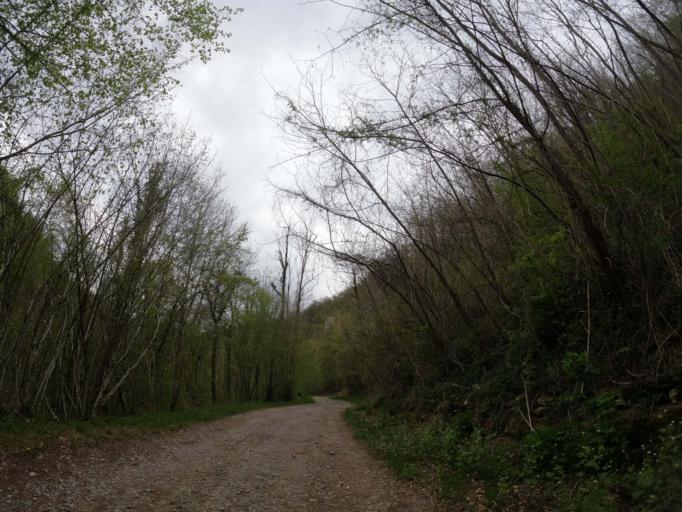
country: IT
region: Friuli Venezia Giulia
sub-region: Provincia di Udine
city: Stregna
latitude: 46.1205
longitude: 13.6150
